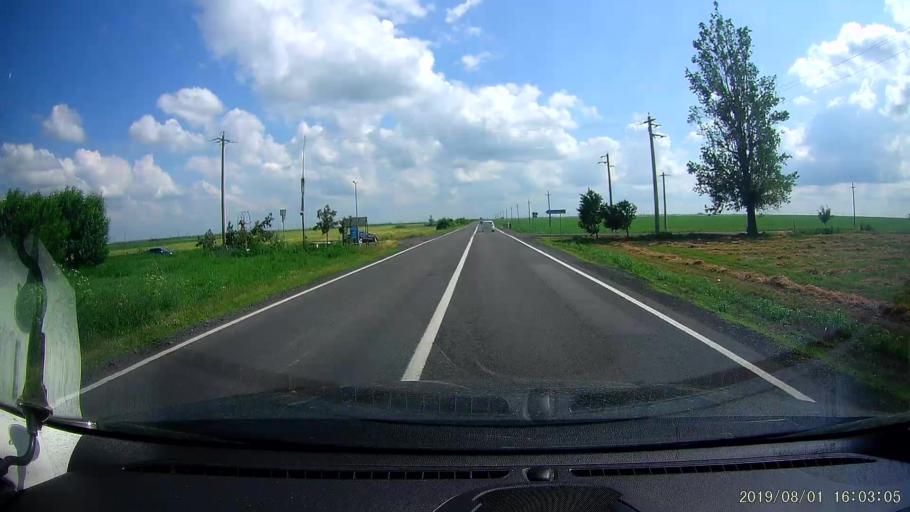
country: RO
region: Calarasi
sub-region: Comuna Dragalina
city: Drajna Noua
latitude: 44.4789
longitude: 27.3855
